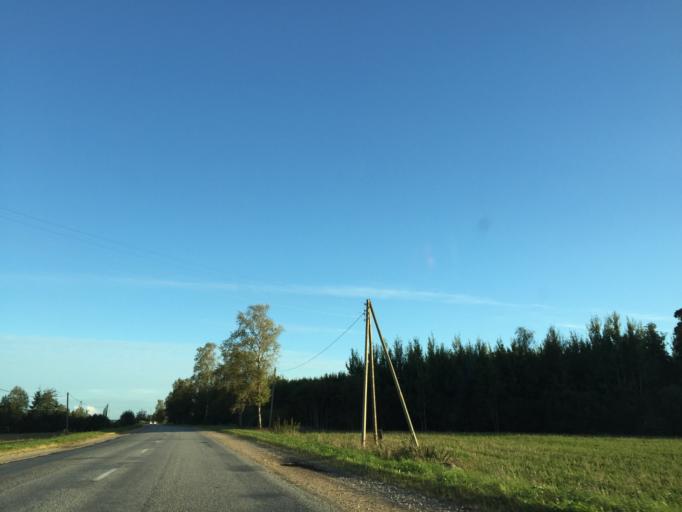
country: LV
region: Saldus Rajons
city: Saldus
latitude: 56.7317
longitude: 22.3778
